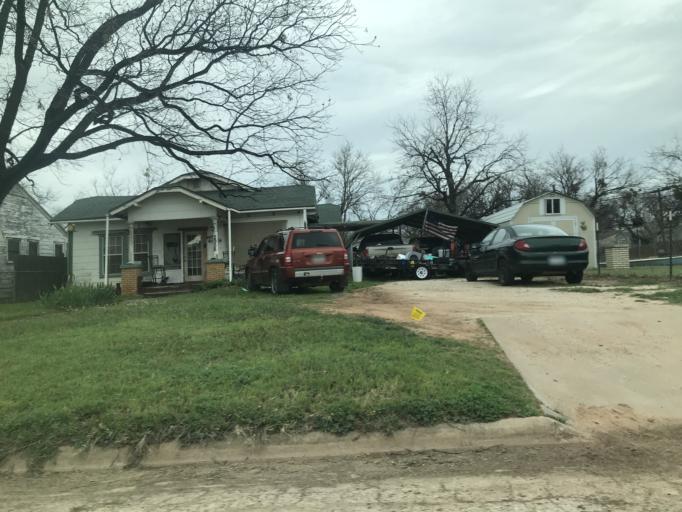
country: US
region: Texas
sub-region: Taylor County
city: Abilene
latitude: 32.4456
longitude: -99.7597
